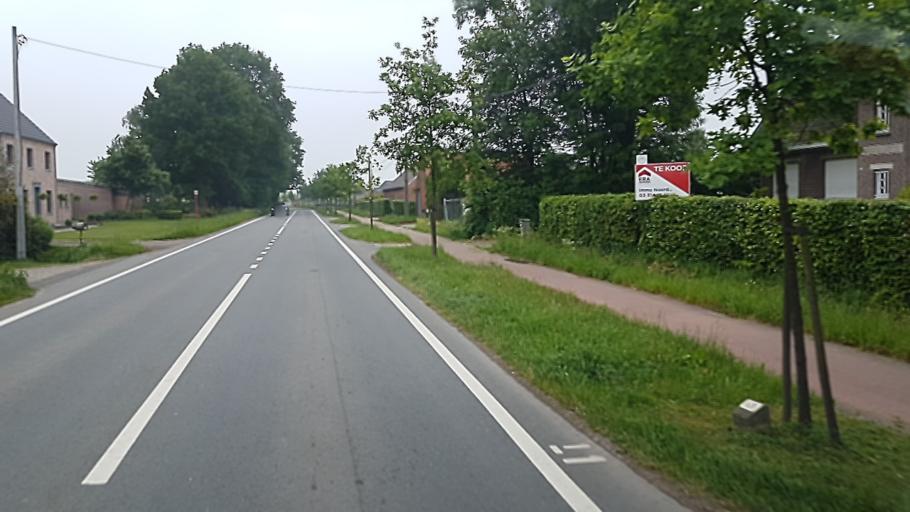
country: BE
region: Flanders
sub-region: Provincie Antwerpen
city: Zoersel
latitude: 51.3051
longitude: 4.6766
